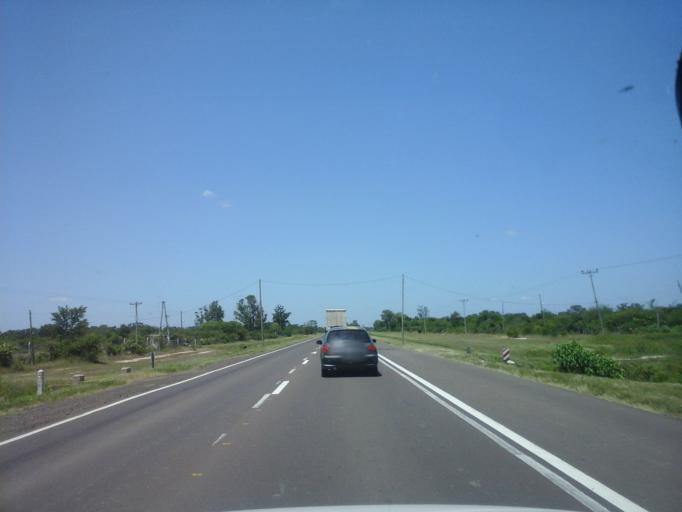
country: AR
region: Corrientes
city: Paso de la Patria
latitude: -27.4077
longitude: -58.6520
